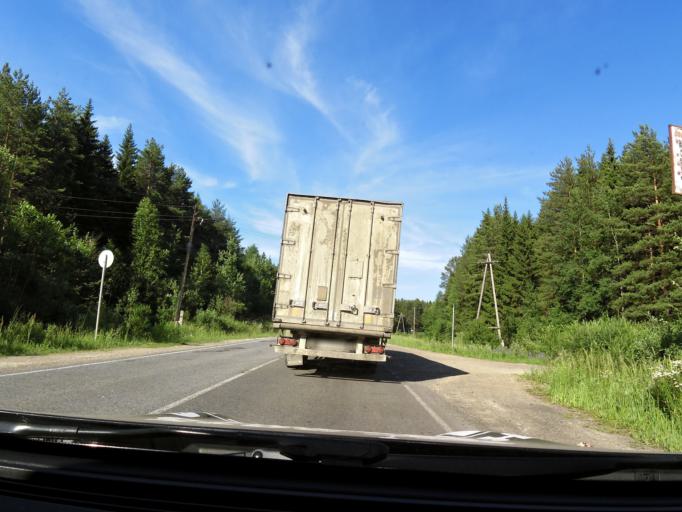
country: RU
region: Kirov
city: Belaya Kholunitsa
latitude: 58.8718
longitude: 50.8488
